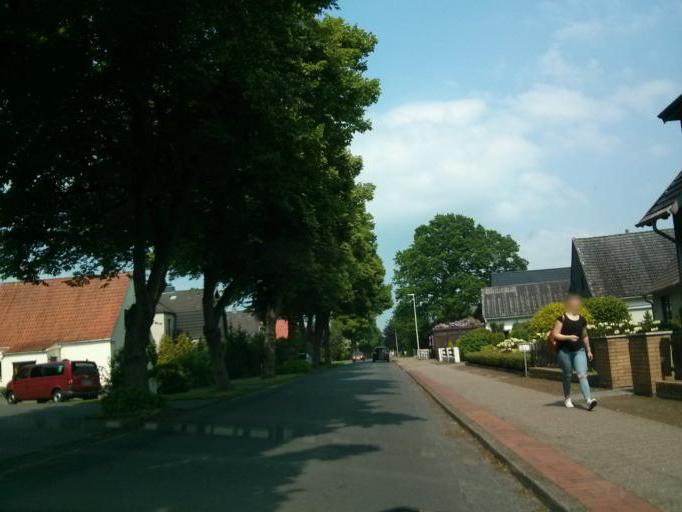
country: DE
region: Lower Saxony
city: Loxstedt
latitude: 53.4853
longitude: 8.6865
